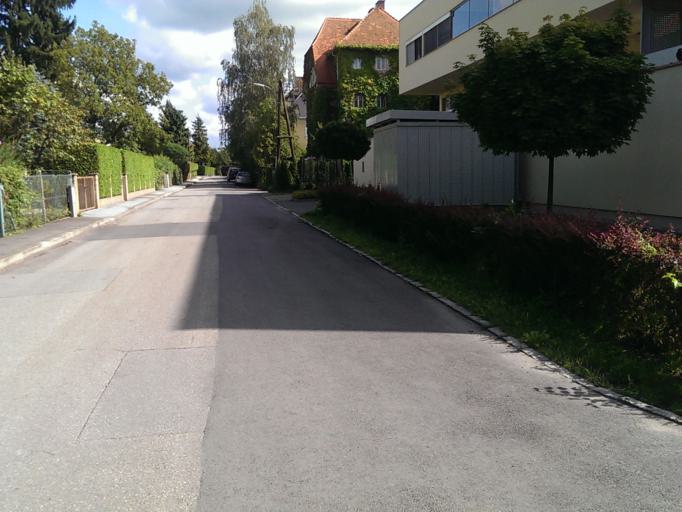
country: AT
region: Styria
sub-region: Graz Stadt
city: Graz
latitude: 47.0570
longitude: 15.4674
